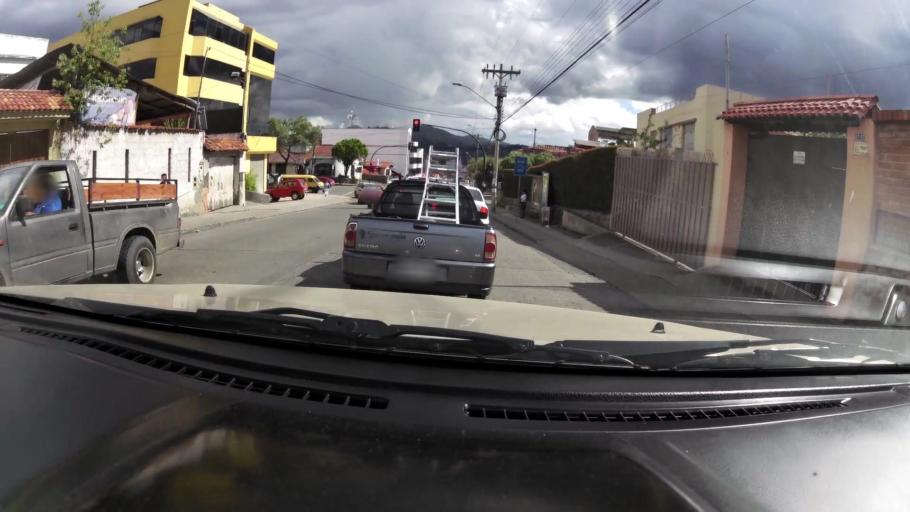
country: EC
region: Azuay
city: Cuenca
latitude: -2.8883
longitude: -79.0024
